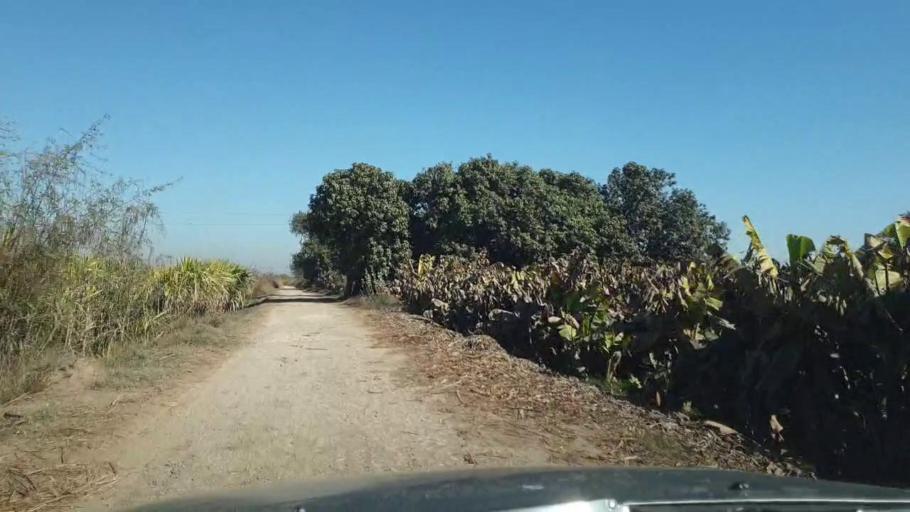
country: PK
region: Sindh
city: Ghotki
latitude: 28.0269
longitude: 69.2869
